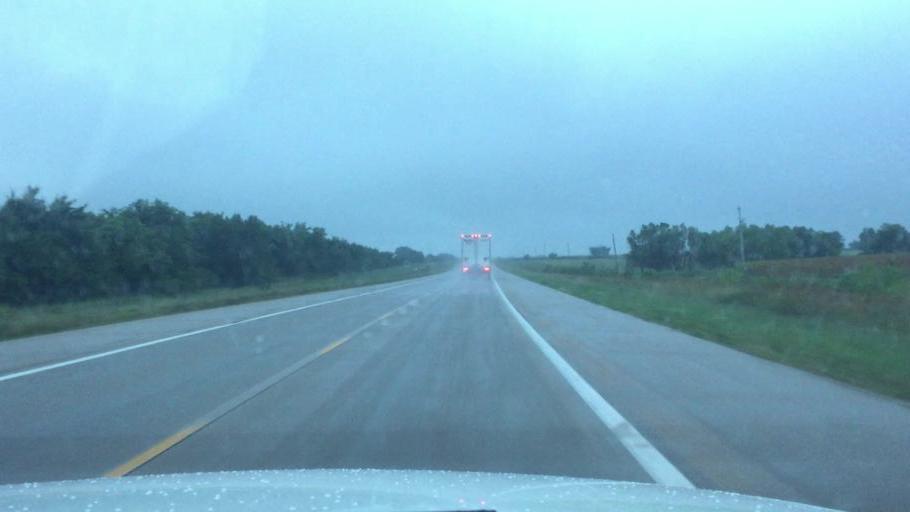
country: US
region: Kansas
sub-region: Neosho County
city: Chanute
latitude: 37.5210
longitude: -95.4710
